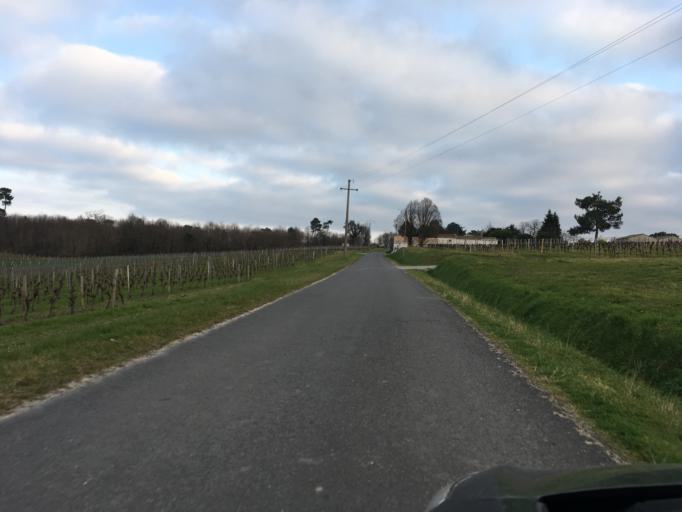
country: FR
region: Aquitaine
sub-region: Departement de la Gironde
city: Saint-Ciers-sur-Gironde
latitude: 45.3132
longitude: -0.6117
